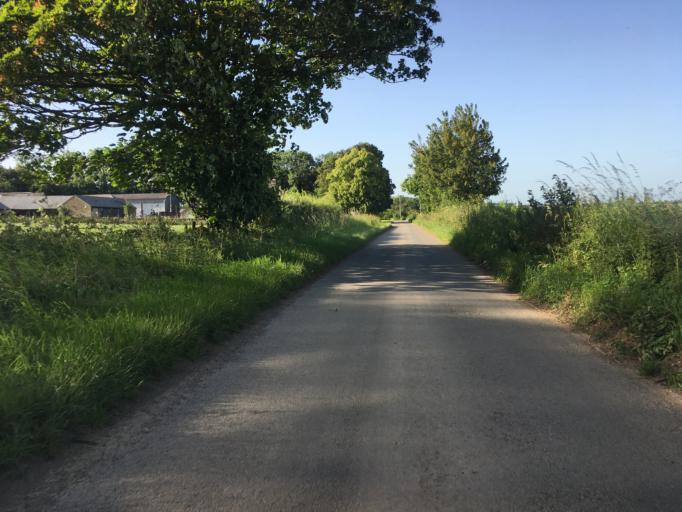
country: GB
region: England
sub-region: Gloucestershire
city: Lechlade
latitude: 51.7521
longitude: -1.7222
